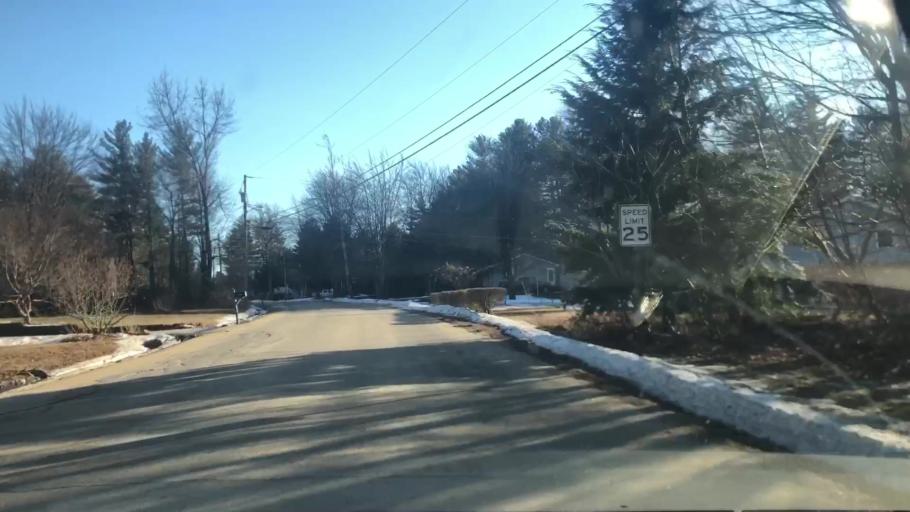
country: US
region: New Hampshire
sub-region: Hillsborough County
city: Milford
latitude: 42.8380
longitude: -71.6742
